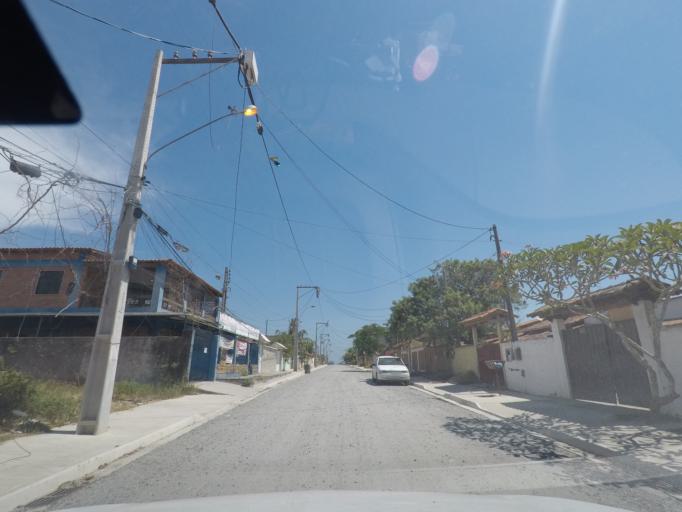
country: BR
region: Rio de Janeiro
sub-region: Marica
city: Marica
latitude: -22.9649
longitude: -42.9558
